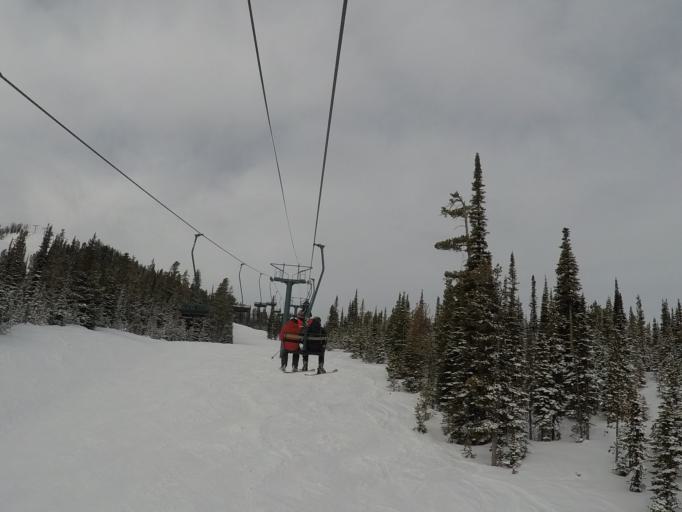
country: US
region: Montana
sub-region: Meagher County
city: White Sulphur Springs
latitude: 46.8396
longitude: -110.7087
